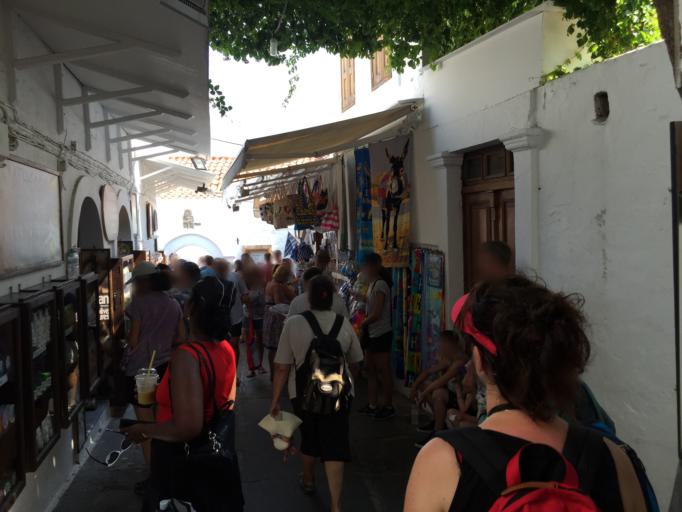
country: GR
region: South Aegean
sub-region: Nomos Dodekanisou
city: Lardos
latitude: 36.0915
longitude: 28.0858
